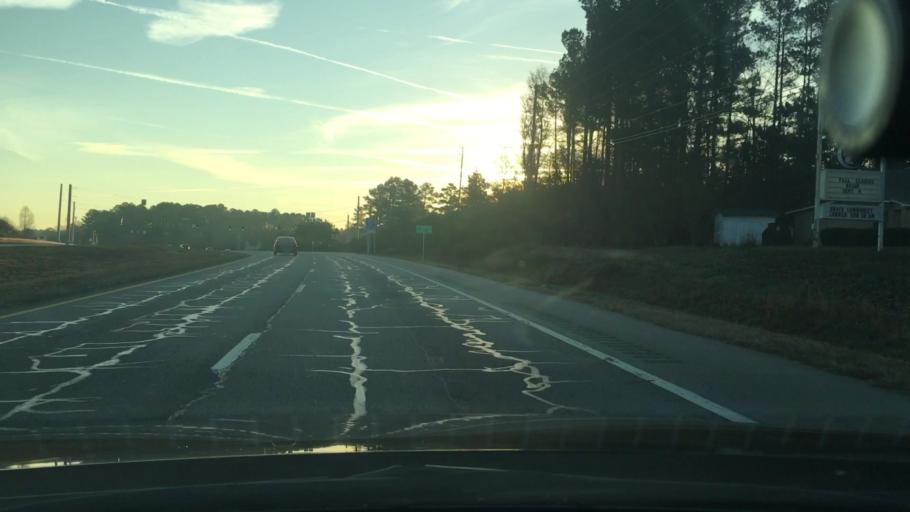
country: US
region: Georgia
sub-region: Fayette County
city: Peachtree City
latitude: 33.3972
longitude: -84.6212
